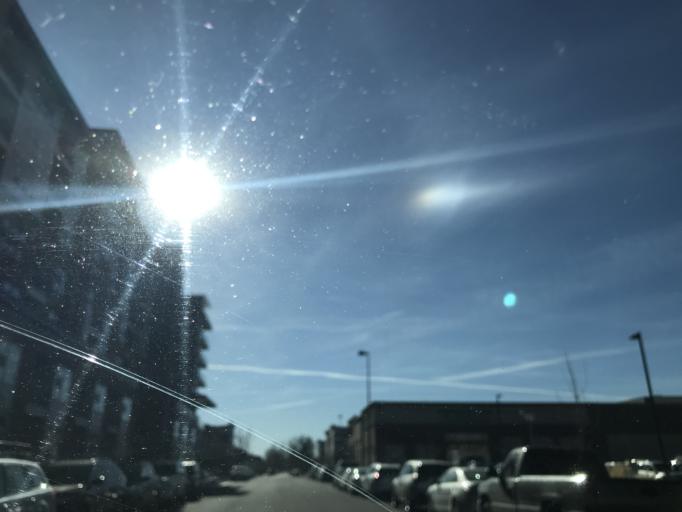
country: US
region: Colorado
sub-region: Denver County
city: Denver
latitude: 39.6979
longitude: -104.9851
